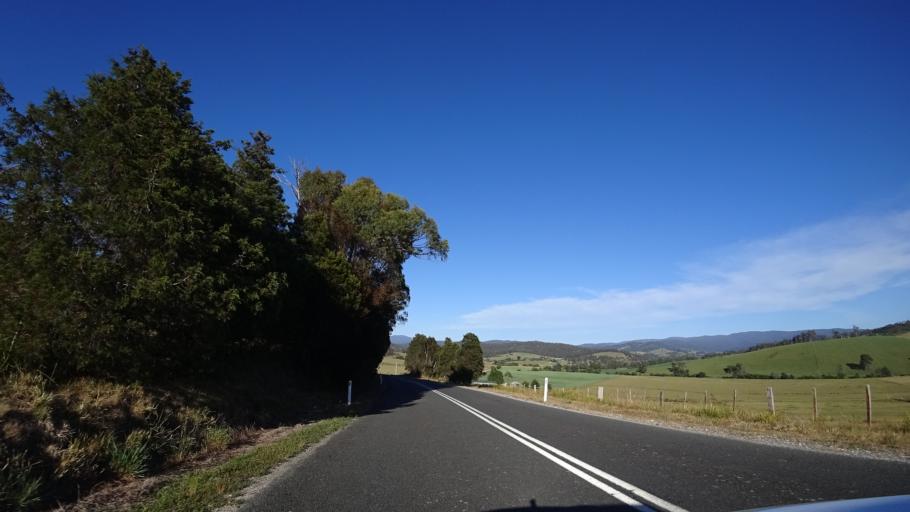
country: AU
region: Tasmania
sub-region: Break O'Day
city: St Helens
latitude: -41.2727
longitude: 148.1158
